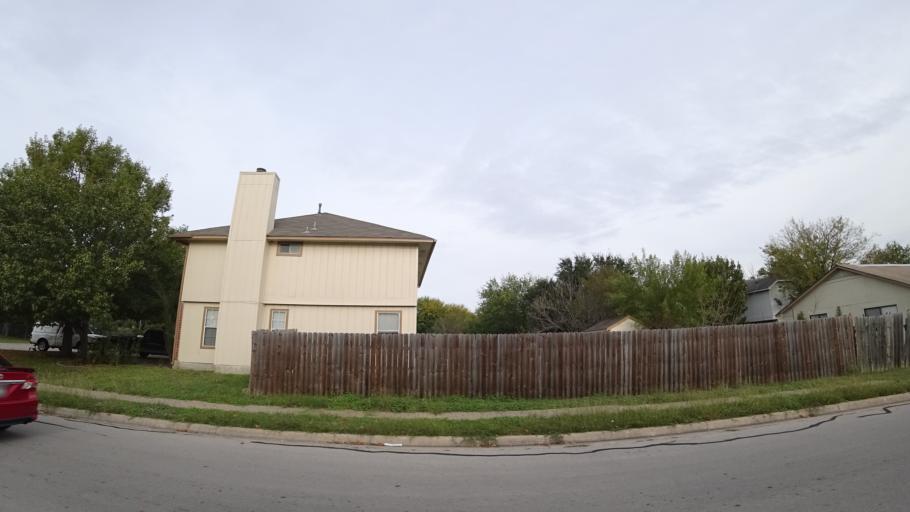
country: US
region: Texas
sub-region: Williamson County
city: Round Rock
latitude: 30.5032
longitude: -97.6659
